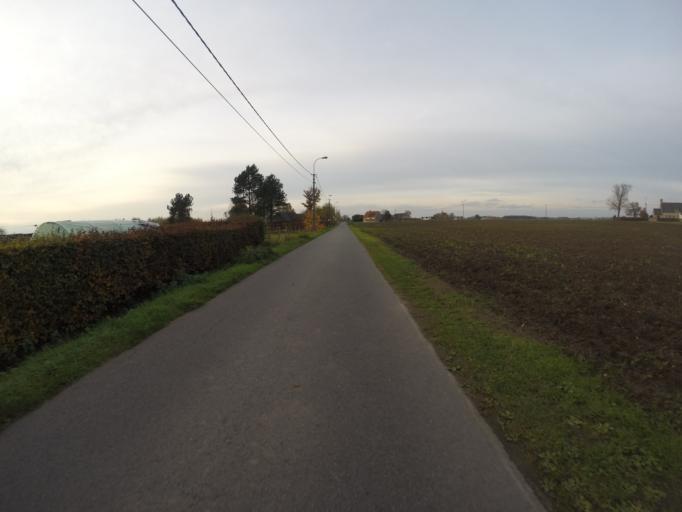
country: BE
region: Flanders
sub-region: Provincie Oost-Vlaanderen
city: Aalter
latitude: 51.0625
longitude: 3.4492
